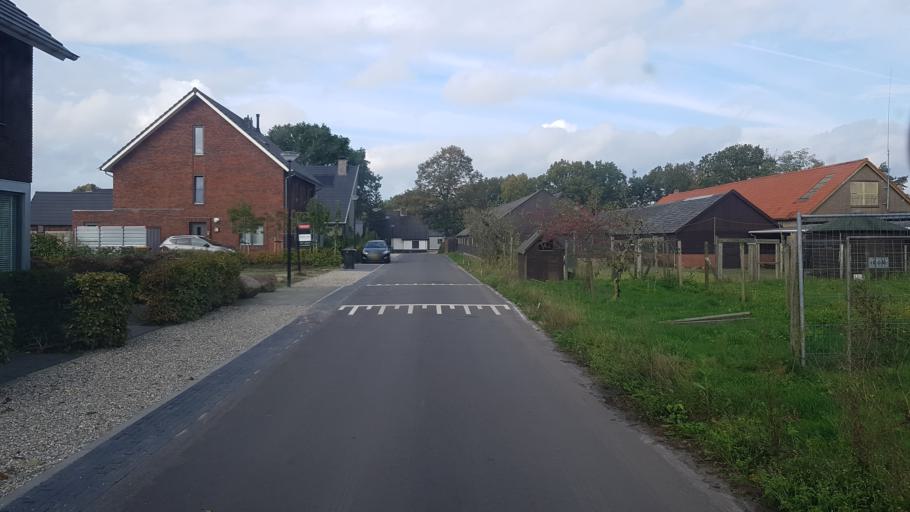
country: NL
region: Gelderland
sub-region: Gemeente Apeldoorn
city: Uddel
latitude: 52.2587
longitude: 5.7860
